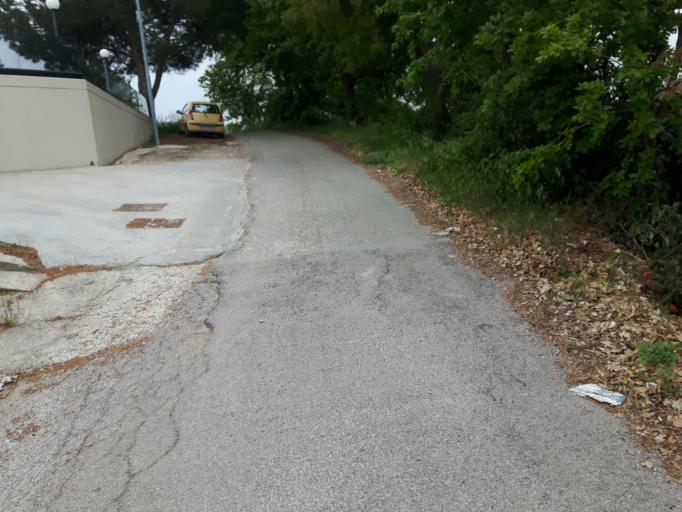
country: IT
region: Abruzzo
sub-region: Provincia di Chieti
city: Vasto
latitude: 42.1422
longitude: 14.6943
